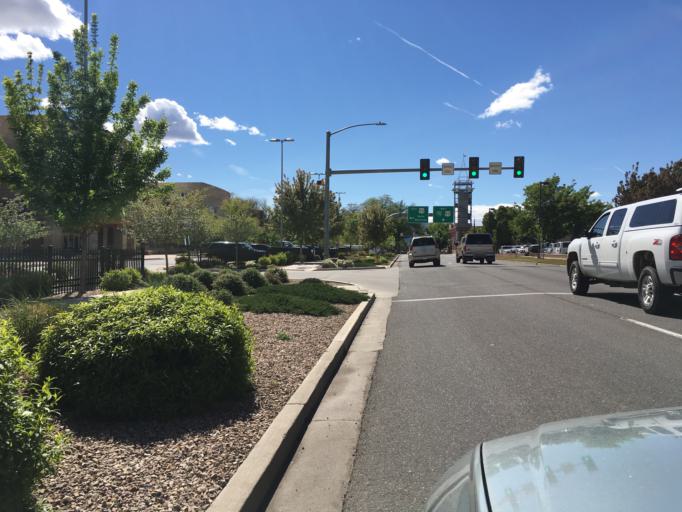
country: US
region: Colorado
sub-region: Mesa County
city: Grand Junction
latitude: 39.0653
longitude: -108.5624
